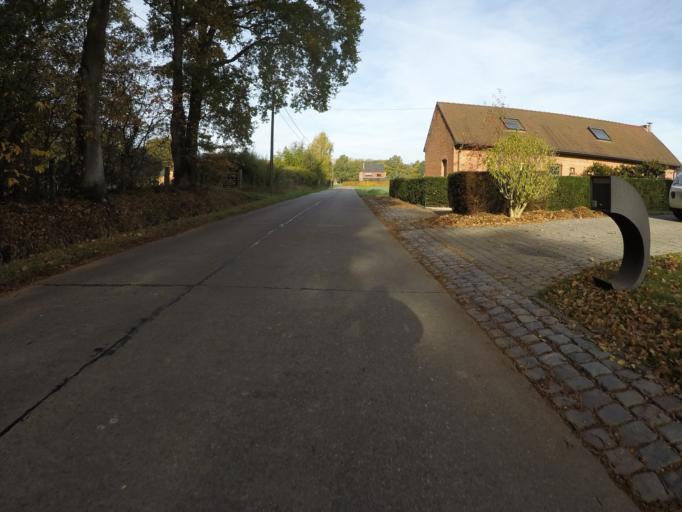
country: BE
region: Flanders
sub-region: Provincie Vlaams-Brabant
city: Begijnendijk
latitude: 51.0050
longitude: 4.7738
